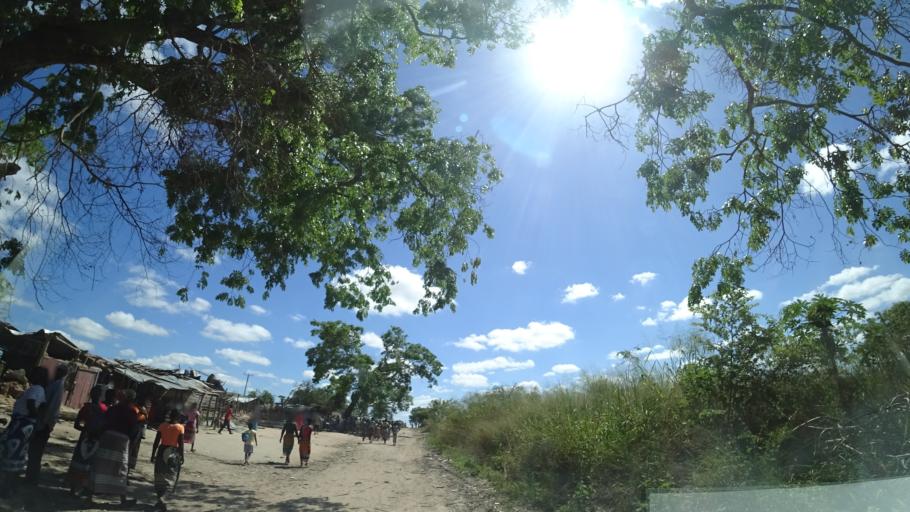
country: MZ
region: Sofala
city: Dondo
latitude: -19.2727
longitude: 34.6797
